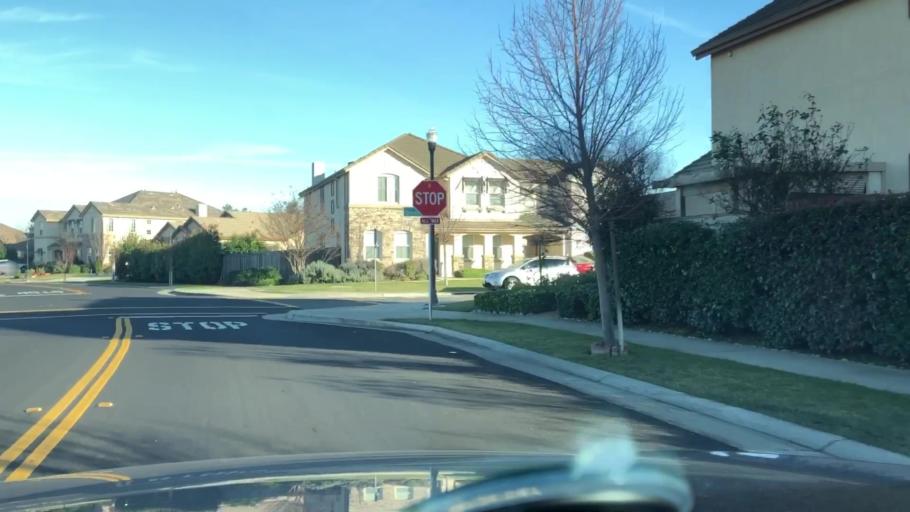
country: US
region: California
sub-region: Sacramento County
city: Laguna
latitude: 38.3984
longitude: -121.4066
